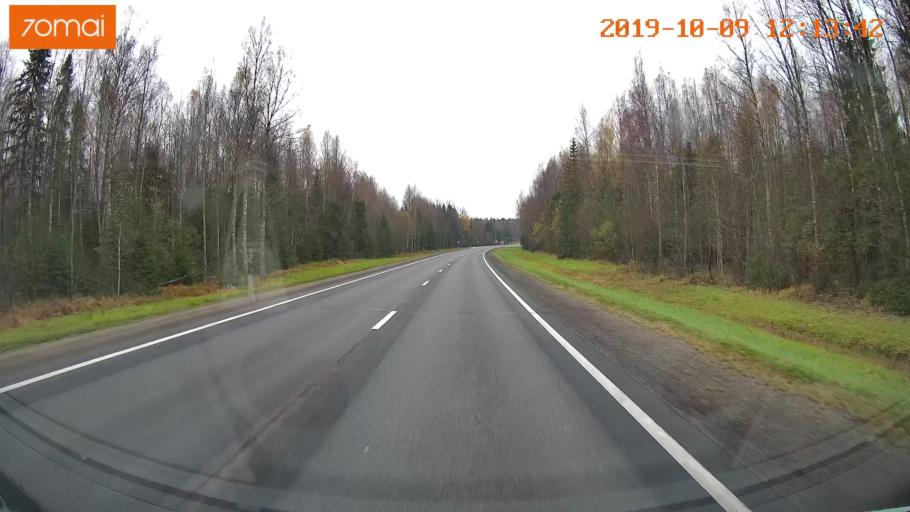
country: RU
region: Jaroslavl
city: Prechistoye
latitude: 58.5065
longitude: 40.3443
